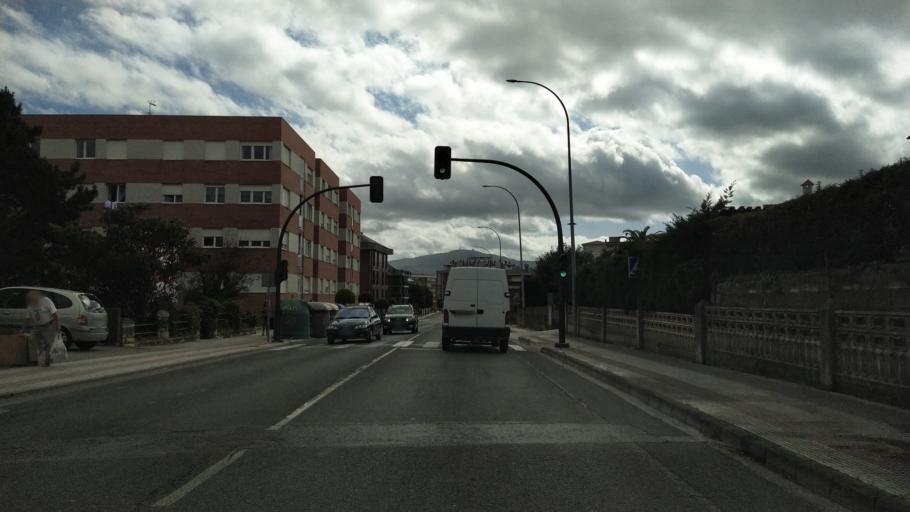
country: ES
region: Cantabria
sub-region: Provincia de Cantabria
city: El Astillero
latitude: 43.4215
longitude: -3.8486
